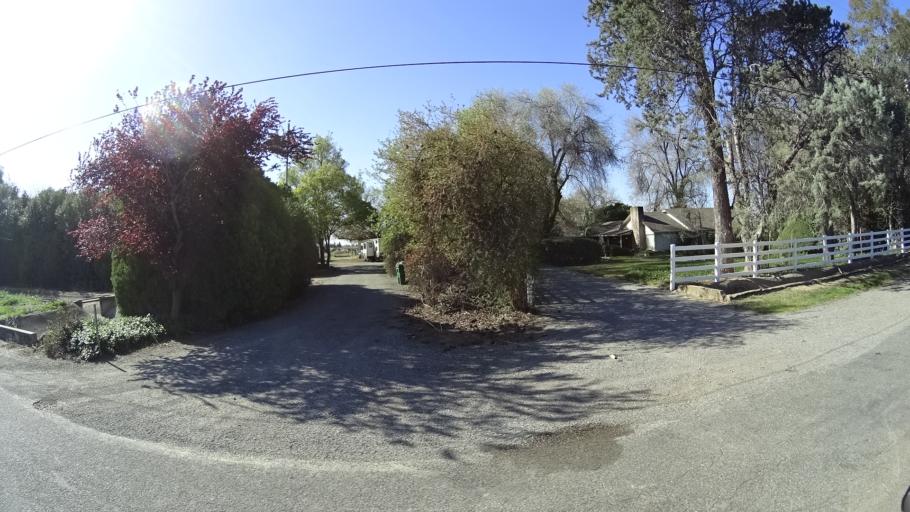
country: US
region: California
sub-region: Glenn County
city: Orland
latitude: 39.7441
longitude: -122.2272
